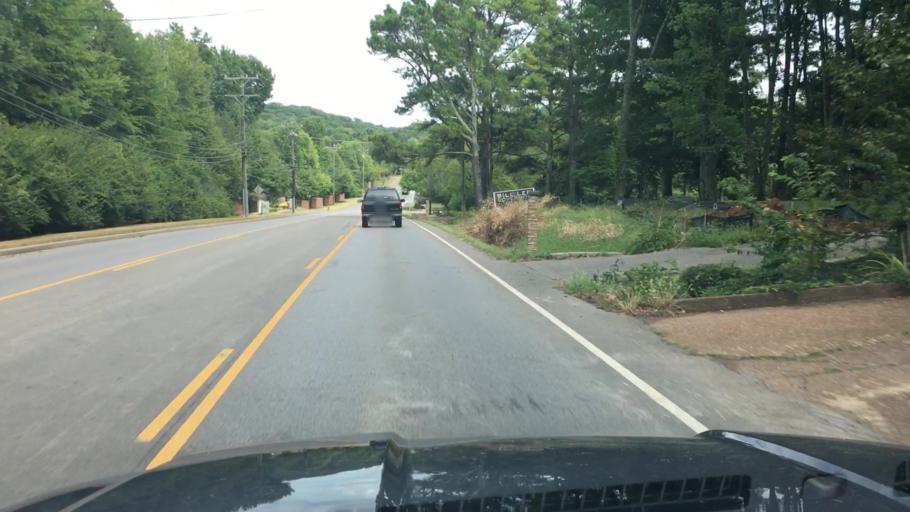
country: US
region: Tennessee
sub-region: Davidson County
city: Forest Hills
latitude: 36.0908
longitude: -86.8216
